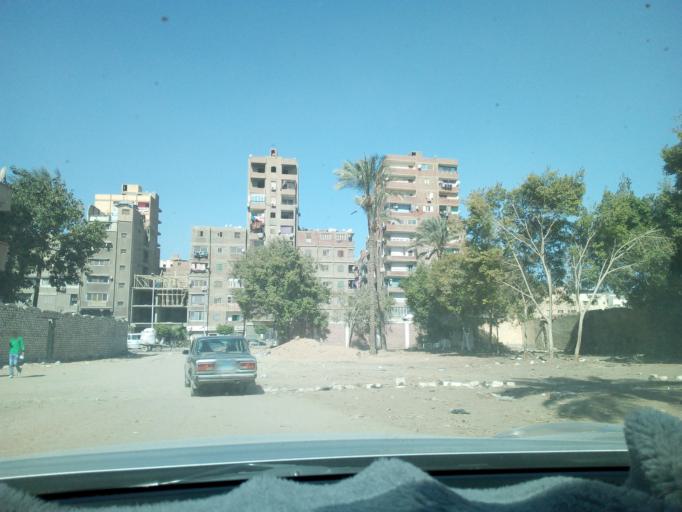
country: EG
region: Muhafazat al Qalyubiyah
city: Al Khankah
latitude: 30.1409
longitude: 31.3348
